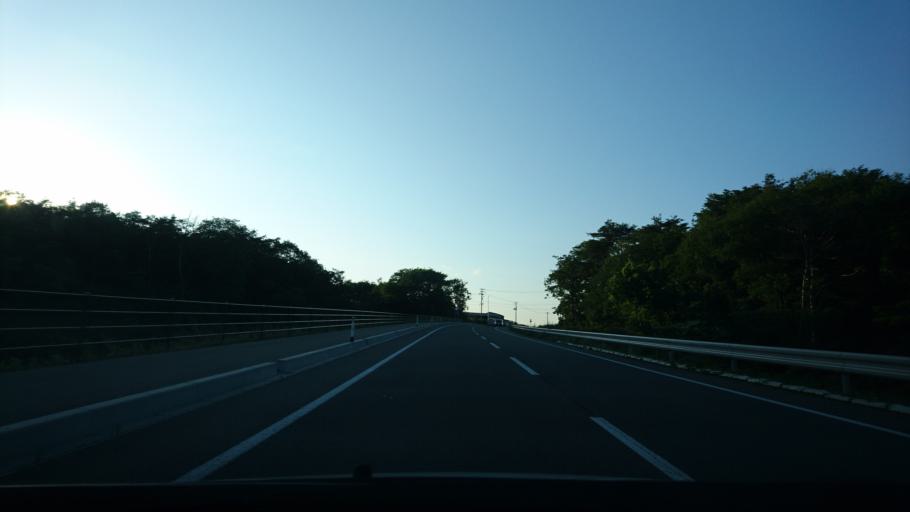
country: JP
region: Iwate
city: Ichinoseki
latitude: 38.8779
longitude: 141.1600
